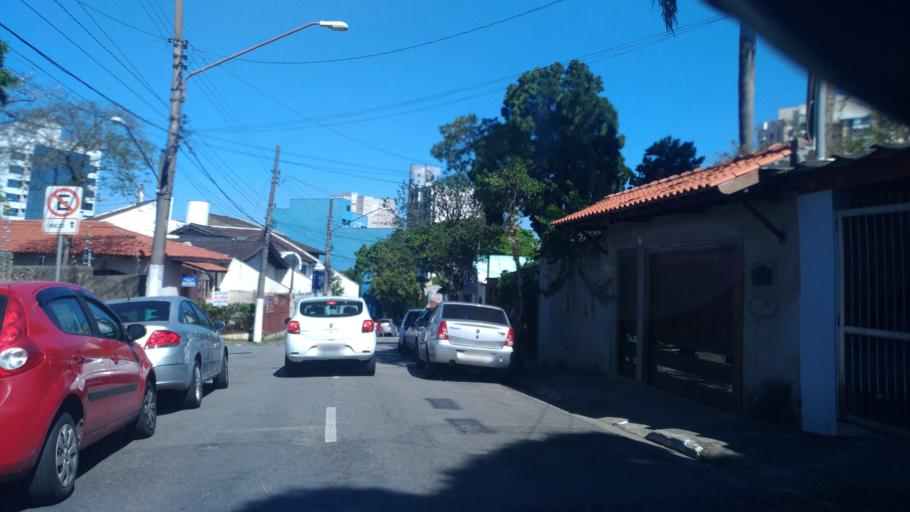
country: BR
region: Sao Paulo
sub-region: Sao Bernardo Do Campo
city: Sao Bernardo do Campo
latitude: -23.6943
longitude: -46.5551
